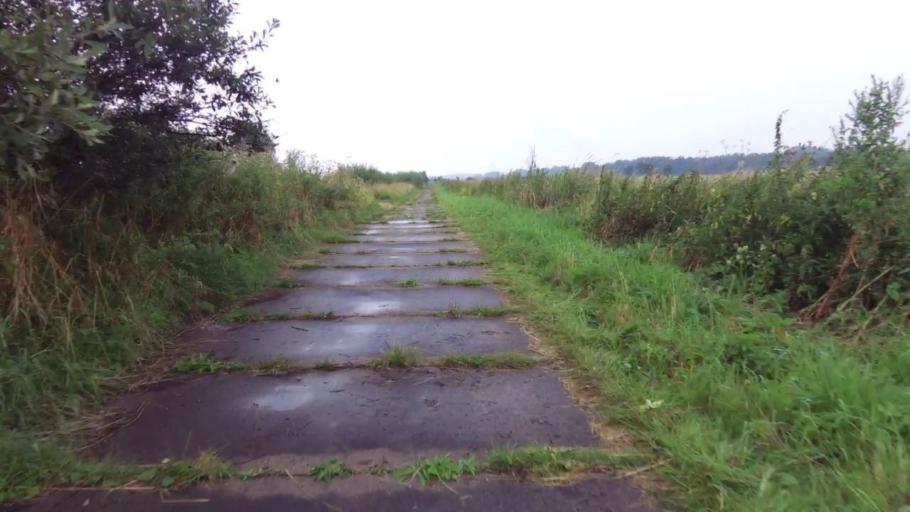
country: PL
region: West Pomeranian Voivodeship
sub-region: Powiat choszczenski
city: Choszczno
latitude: 53.2465
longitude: 15.4253
